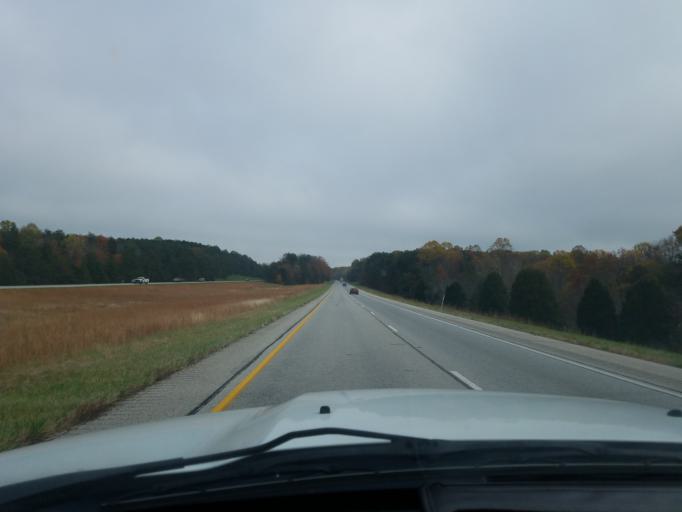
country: US
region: Indiana
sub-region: Floyd County
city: Georgetown
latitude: 38.2531
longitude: -86.0355
